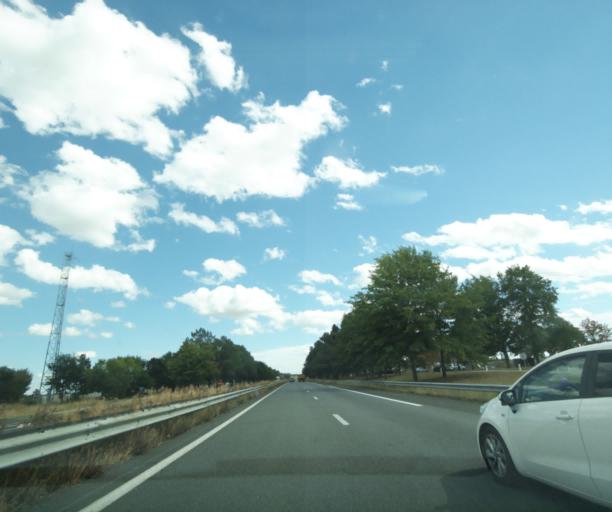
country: FR
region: Aquitaine
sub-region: Departement du Lot-et-Garonne
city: Meilhan-sur-Garonne
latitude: 44.4755
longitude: 0.0354
